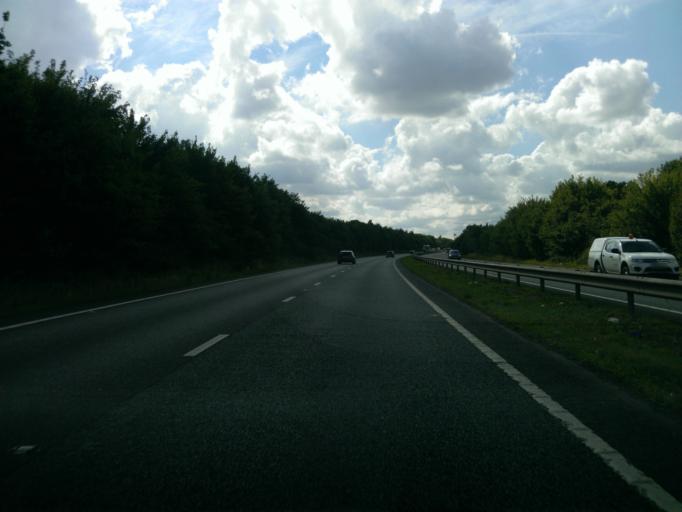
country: GB
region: England
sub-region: Northamptonshire
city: Desborough
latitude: 52.4053
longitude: -0.8505
